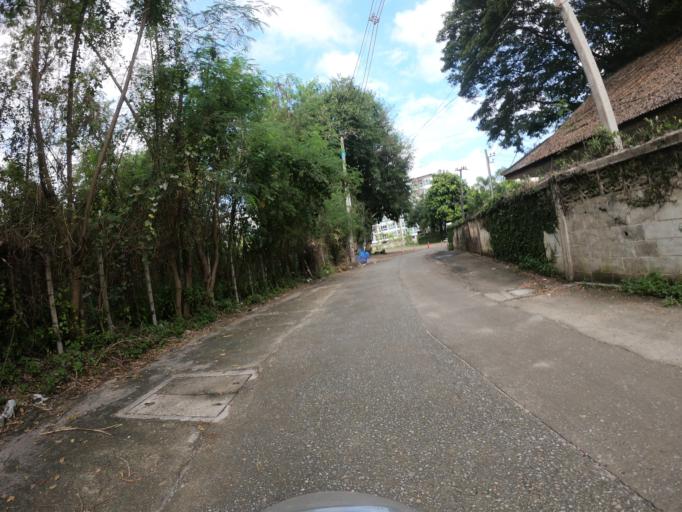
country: TH
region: Chiang Mai
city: Chiang Mai
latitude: 18.8114
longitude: 98.9717
